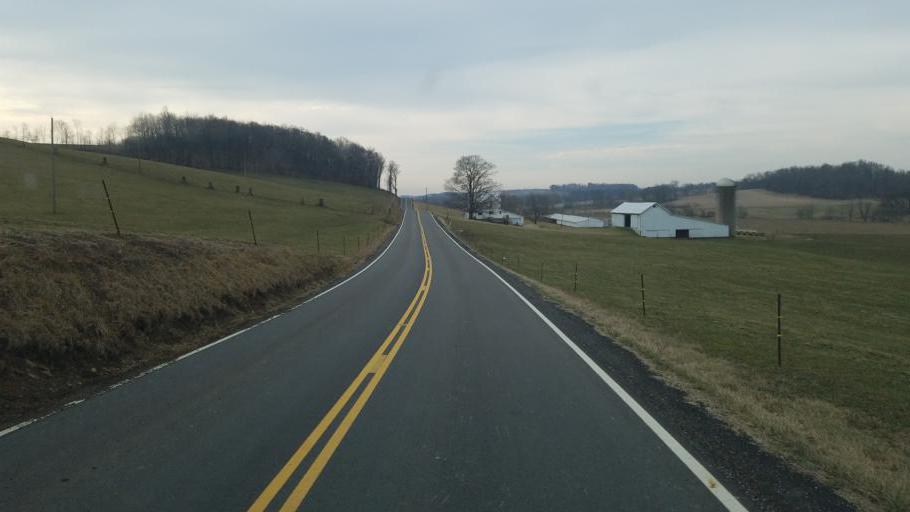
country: US
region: Ohio
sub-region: Knox County
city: Danville
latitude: 40.5265
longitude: -82.3002
